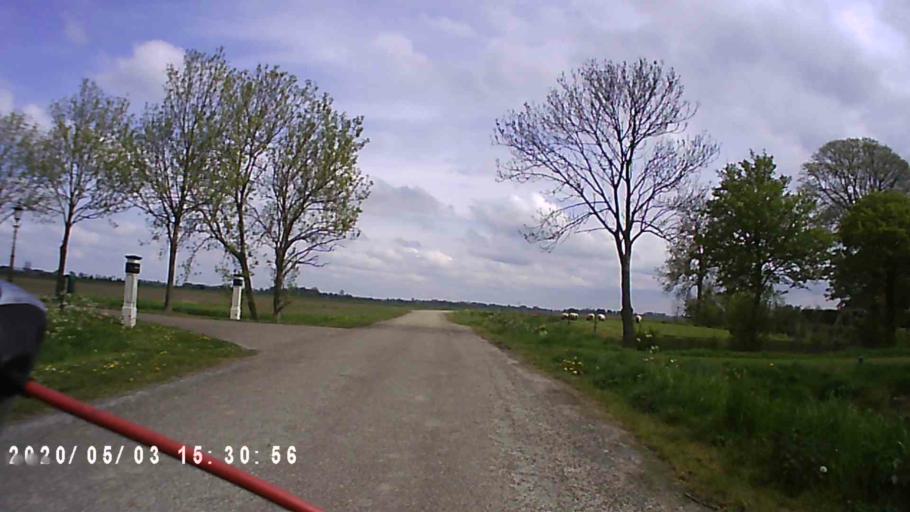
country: NL
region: Groningen
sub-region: Gemeente Winsum
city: Winsum
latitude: 53.3452
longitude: 6.4680
